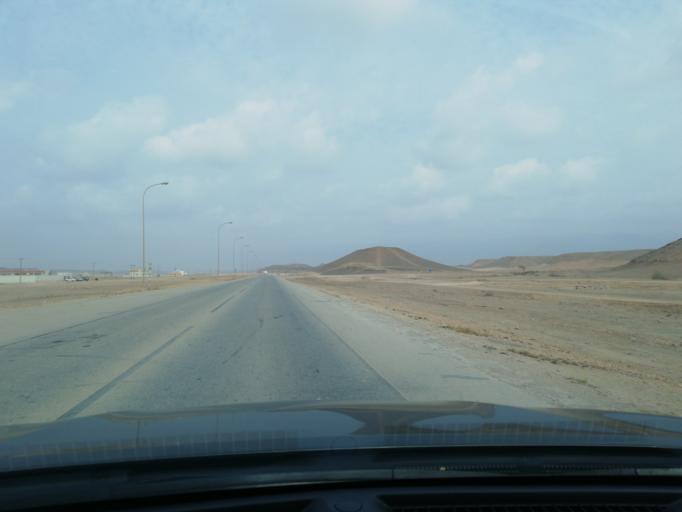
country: OM
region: Zufar
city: Salalah
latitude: 16.9487
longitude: 53.9401
